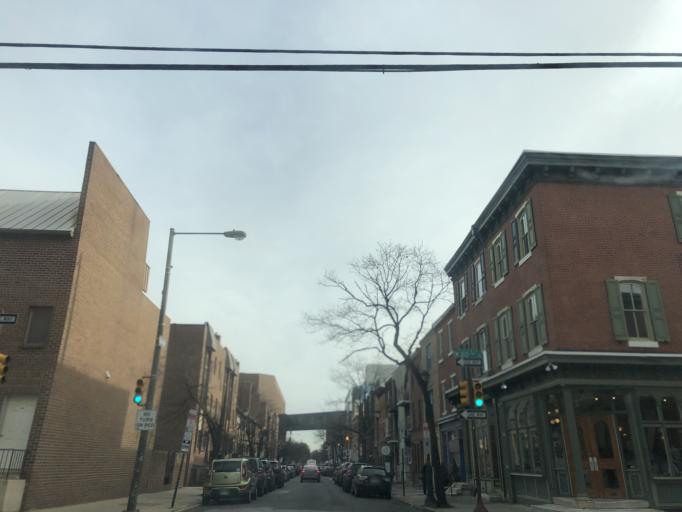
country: US
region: Pennsylvania
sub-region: Philadelphia County
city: Philadelphia
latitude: 39.9448
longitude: -75.1752
